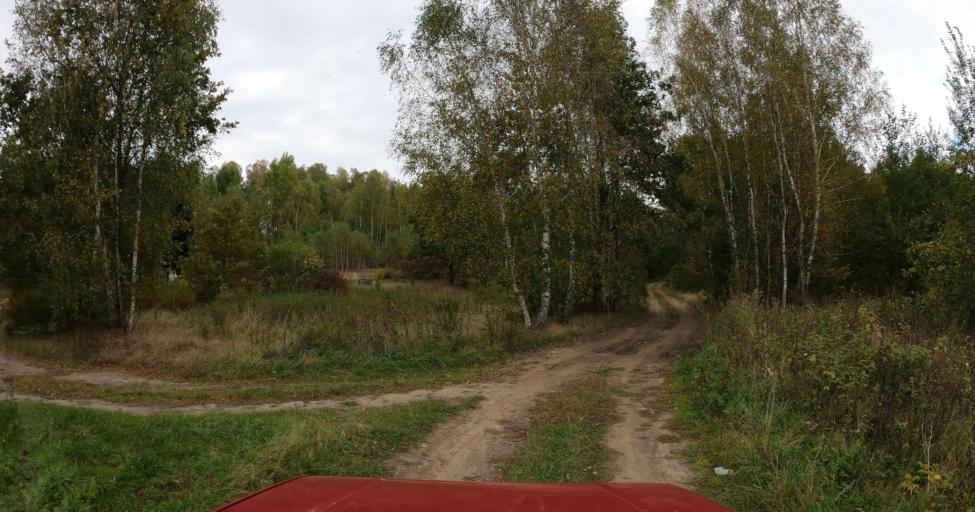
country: PL
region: West Pomeranian Voivodeship
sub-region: Powiat koszalinski
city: Polanow
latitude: 54.1140
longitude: 16.5099
